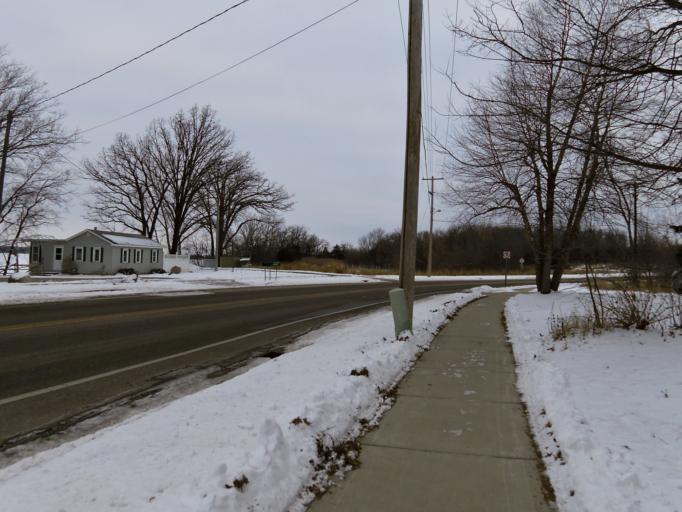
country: US
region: Minnesota
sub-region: Scott County
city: Prior Lake
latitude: 44.7069
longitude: -93.4699
